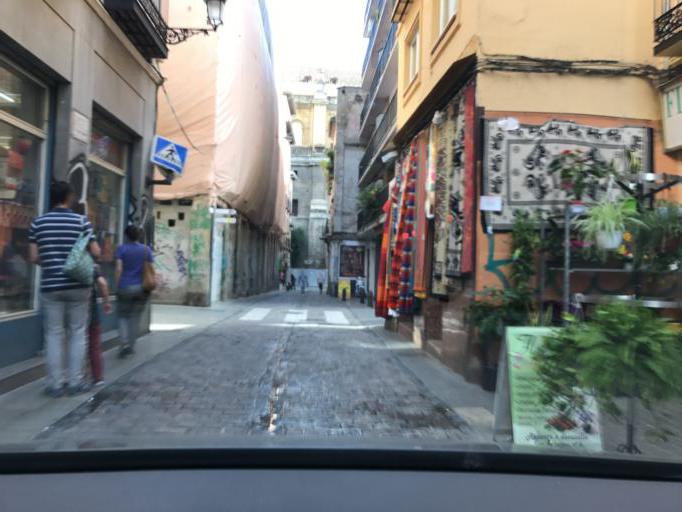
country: ES
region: Andalusia
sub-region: Provincia de Granada
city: Granada
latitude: 37.1773
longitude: -3.6001
